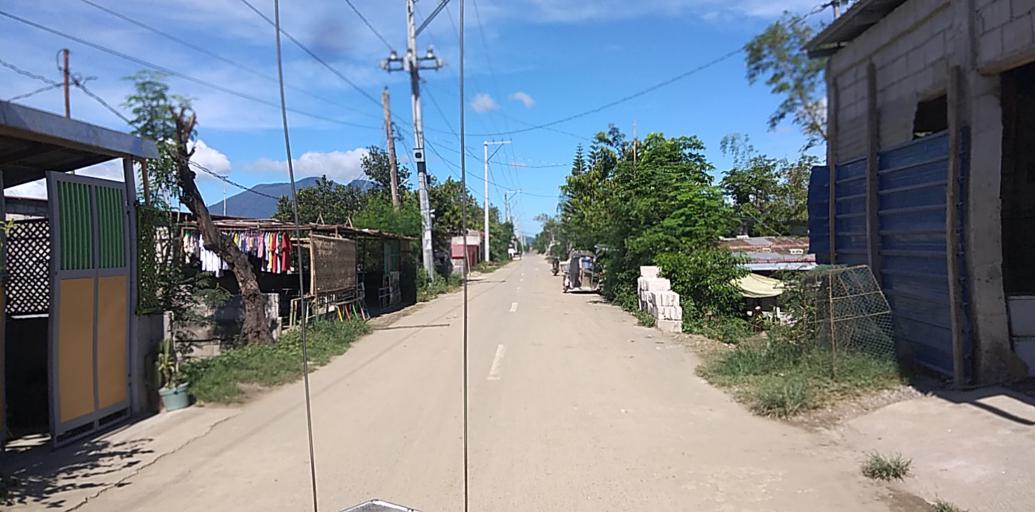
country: PH
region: Central Luzon
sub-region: Province of Pampanga
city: Candating
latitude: 15.1275
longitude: 120.8100
